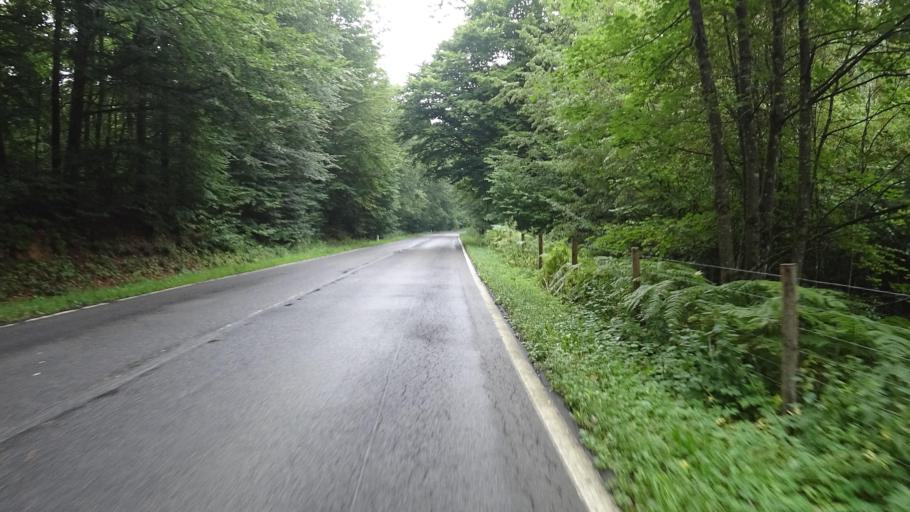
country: BE
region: Wallonia
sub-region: Province du Luxembourg
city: Chiny
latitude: 49.7846
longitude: 5.3304
